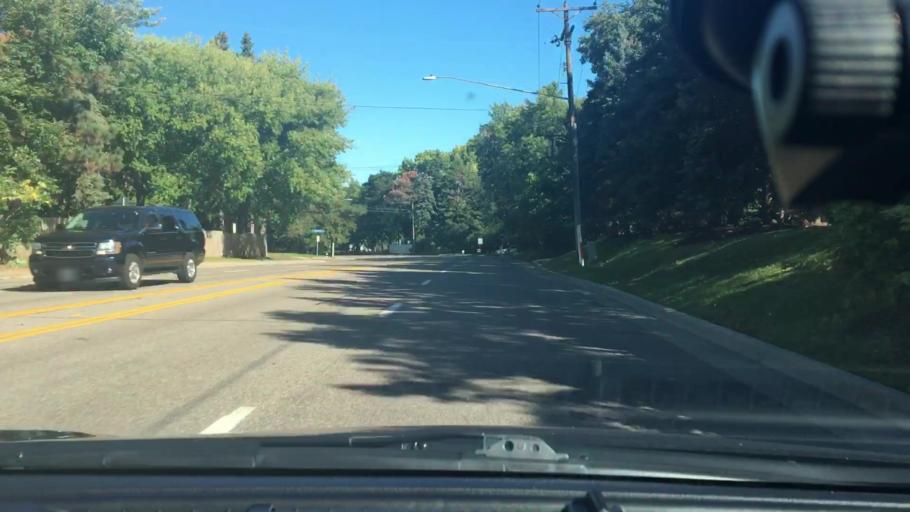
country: US
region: Minnesota
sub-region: Hennepin County
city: Minnetonka Mills
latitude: 44.9740
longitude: -93.4463
